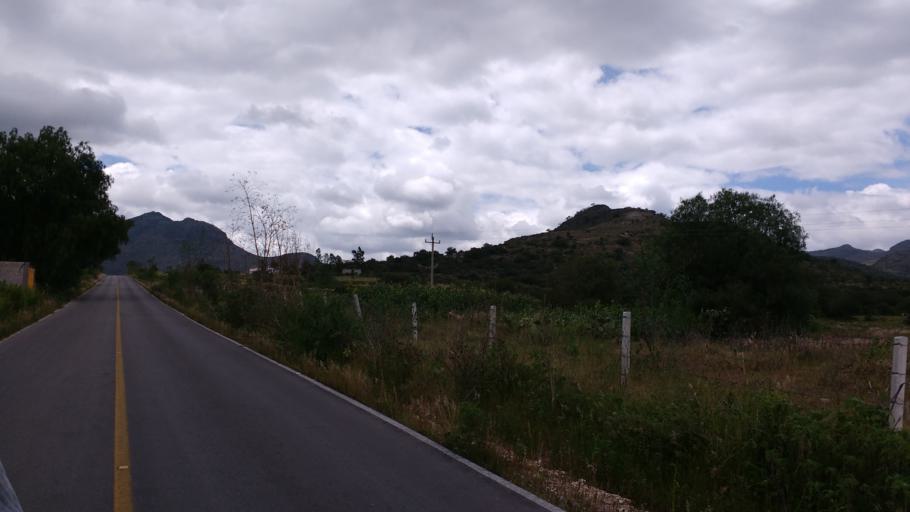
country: MX
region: Hidalgo
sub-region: Tezontepec de Aldama
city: Tenango
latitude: 20.2292
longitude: -99.2706
